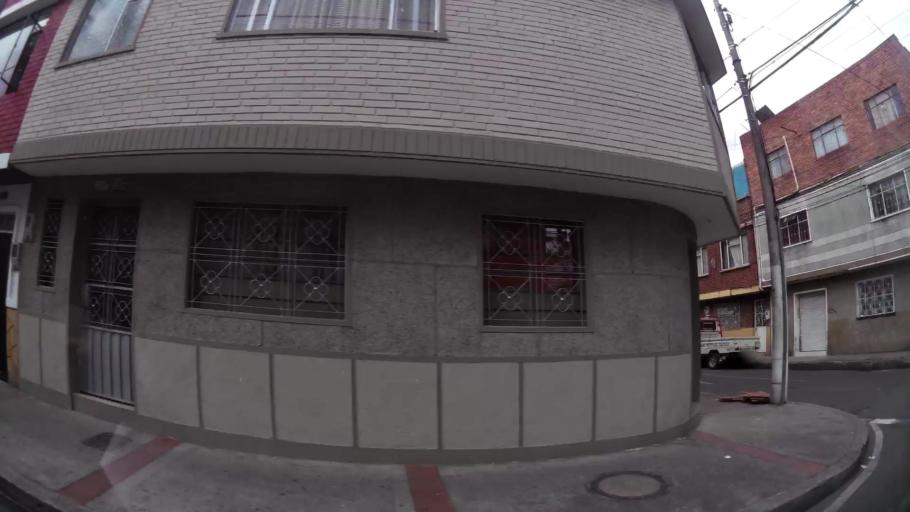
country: CO
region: Bogota D.C.
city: Bogota
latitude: 4.6770
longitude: -74.0930
